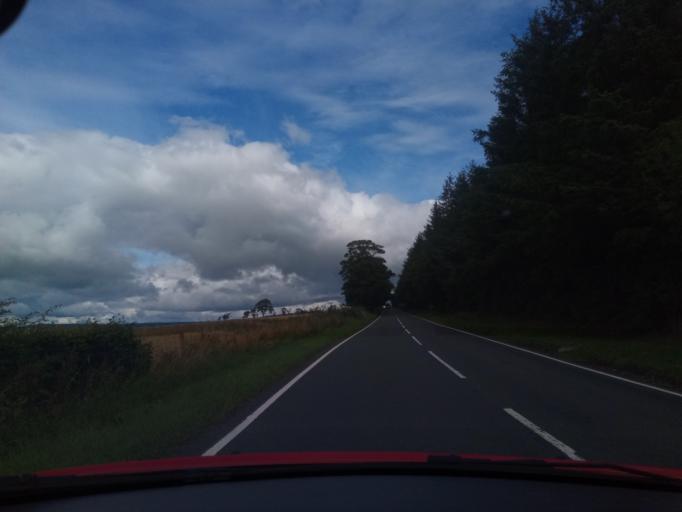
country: GB
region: Scotland
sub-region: The Scottish Borders
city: Lauder
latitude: 55.7348
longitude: -2.7386
